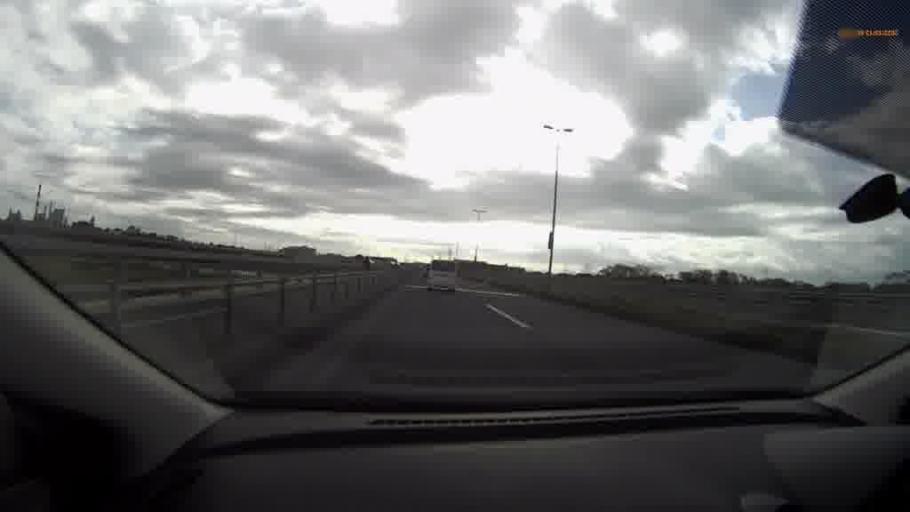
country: JP
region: Hokkaido
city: Kushiro
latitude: 43.0115
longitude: 144.2669
